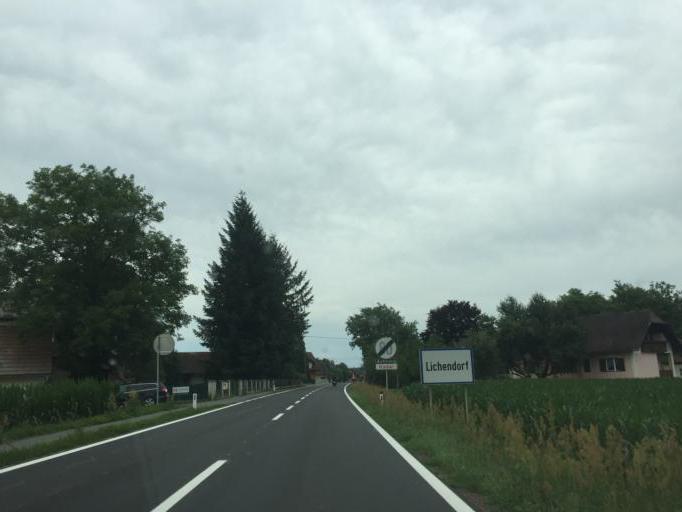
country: SI
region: Sentilj
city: Selnica ob Muri
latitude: 46.7145
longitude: 15.6881
